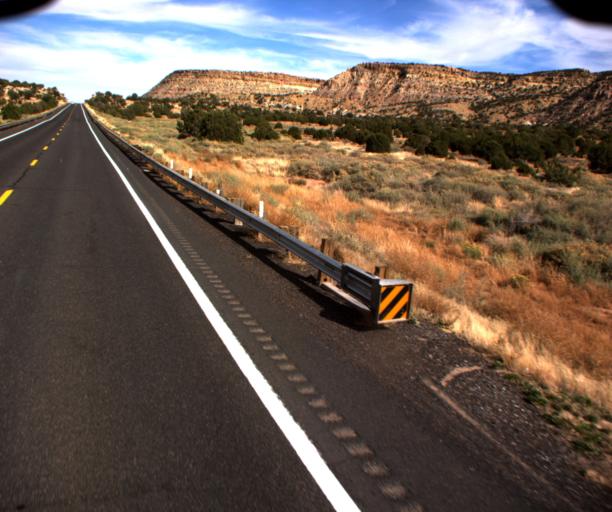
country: US
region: Arizona
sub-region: Navajo County
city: Kayenta
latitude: 36.6804
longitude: -110.3870
